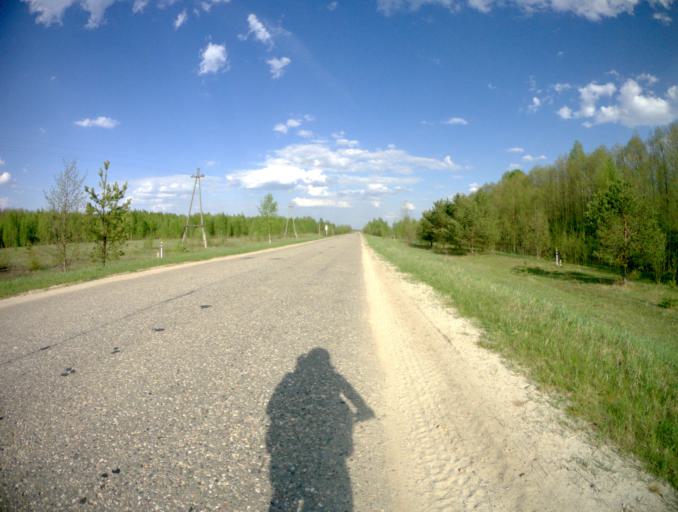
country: RU
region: Ivanovo
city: Kolobovo
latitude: 56.5397
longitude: 41.5103
